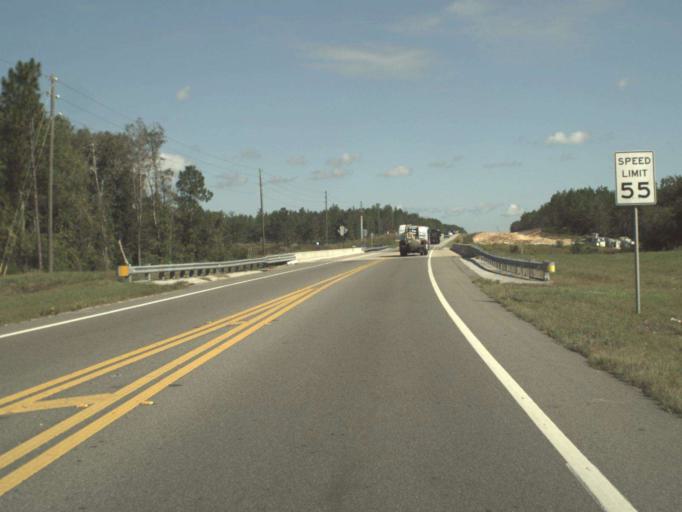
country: US
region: Florida
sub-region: Walton County
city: Freeport
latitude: 30.4953
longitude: -86.1197
